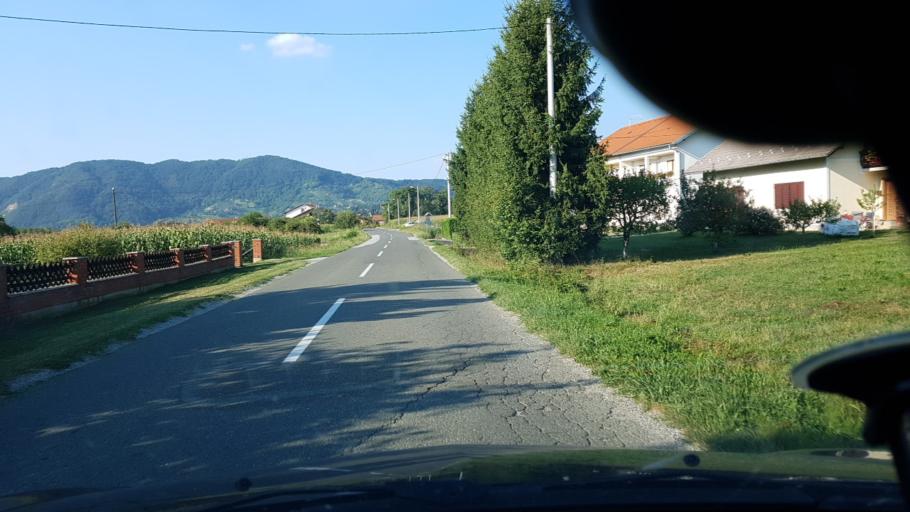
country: SI
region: Bistrica ob Sotli
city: Bistrica ob Sotli
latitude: 46.0267
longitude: 15.7310
